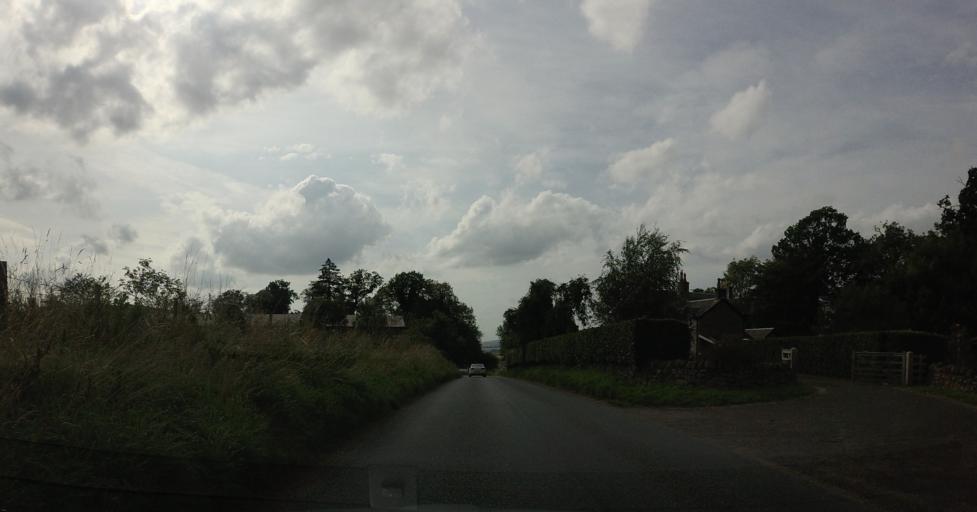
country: GB
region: Scotland
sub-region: Perth and Kinross
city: Methven
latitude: 56.3879
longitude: -3.6034
